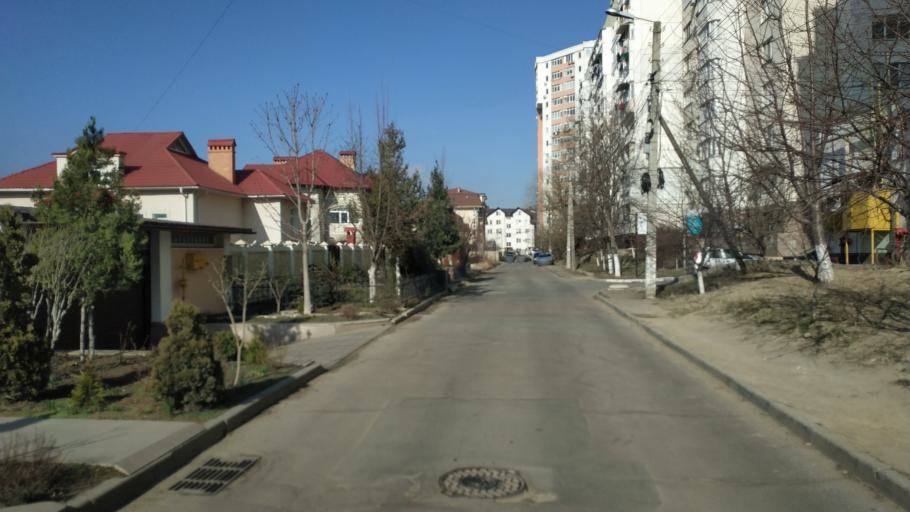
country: MD
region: Chisinau
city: Vatra
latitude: 47.0404
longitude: 28.7610
